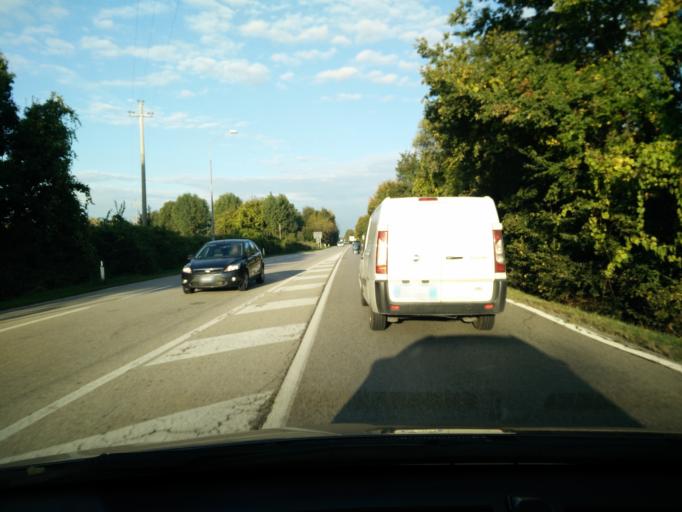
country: IT
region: Veneto
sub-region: Provincia di Treviso
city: Monastier di Treviso
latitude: 45.6374
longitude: 12.4030
